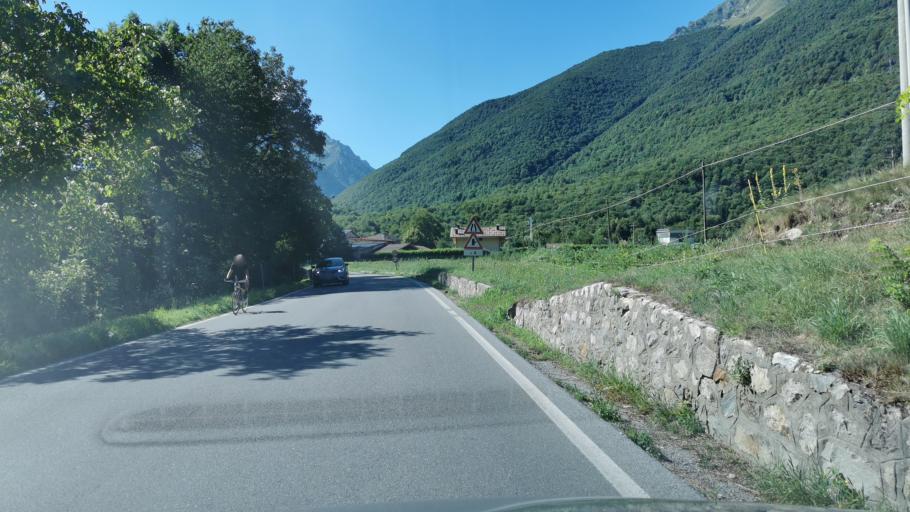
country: IT
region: Piedmont
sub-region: Provincia di Cuneo
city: Valdieri
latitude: 44.2609
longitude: 7.3817
